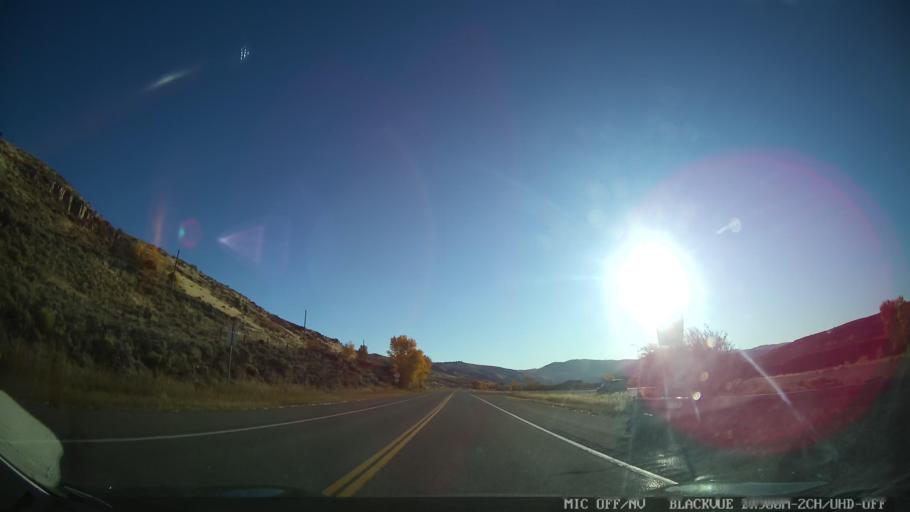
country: US
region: Colorado
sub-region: Grand County
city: Hot Sulphur Springs
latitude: 40.0512
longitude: -106.1679
